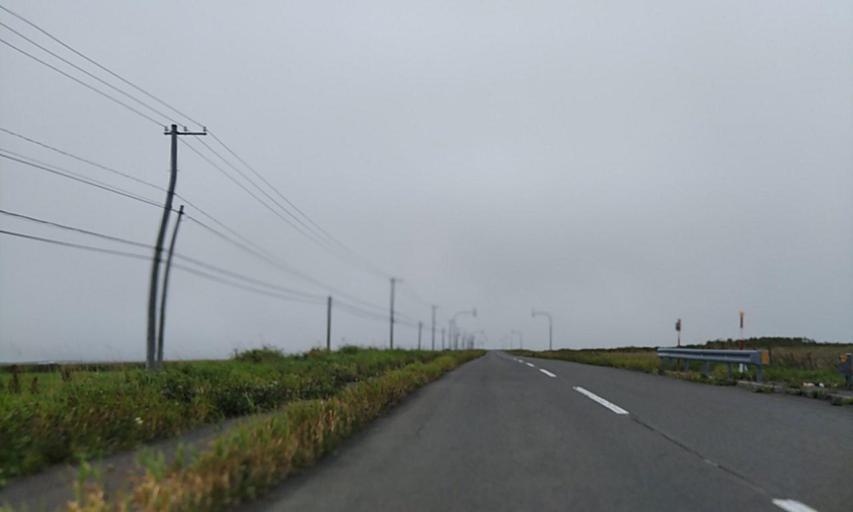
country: JP
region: Hokkaido
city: Nemuro
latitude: 43.3820
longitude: 145.7082
